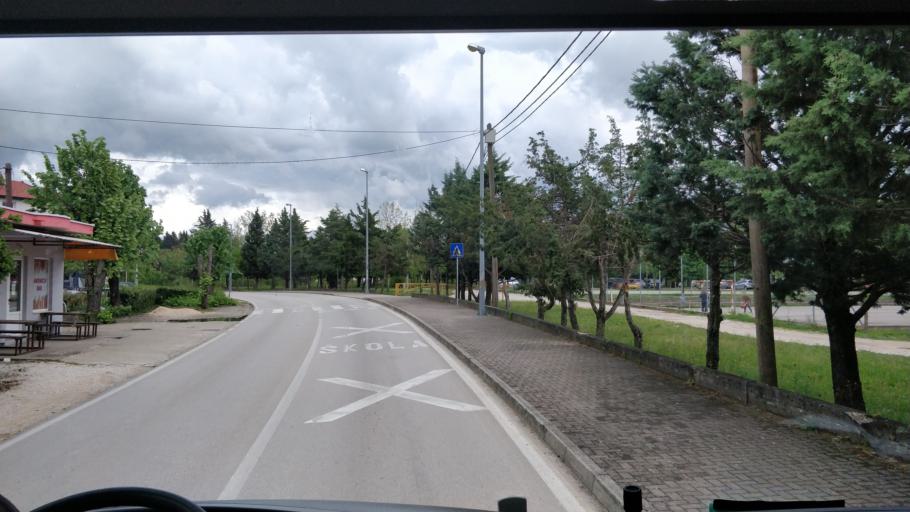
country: BA
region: Federation of Bosnia and Herzegovina
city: Ljubuski
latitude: 43.1834
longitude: 17.5257
